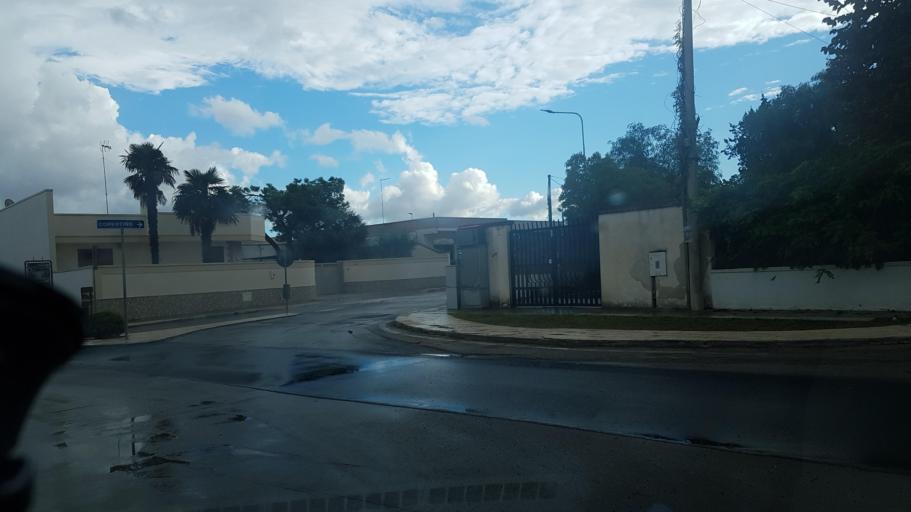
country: IT
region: Apulia
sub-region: Provincia di Lecce
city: Carmiano
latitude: 40.3385
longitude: 18.0415
